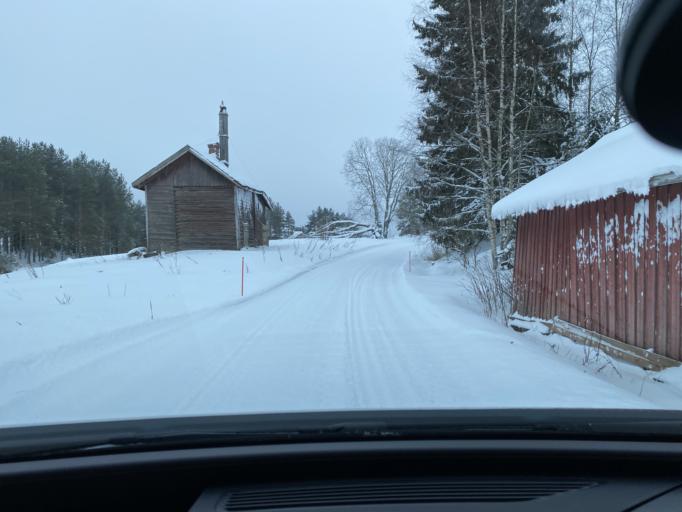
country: FI
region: Pirkanmaa
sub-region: Lounais-Pirkanmaa
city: Punkalaidun
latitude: 61.1244
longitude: 23.0812
